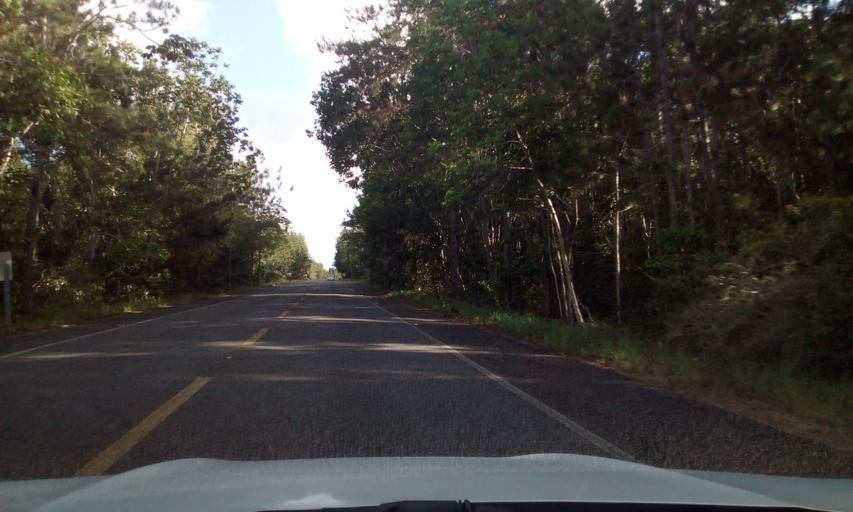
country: BR
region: Bahia
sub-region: Conde
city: Conde
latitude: -12.1077
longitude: -37.7841
